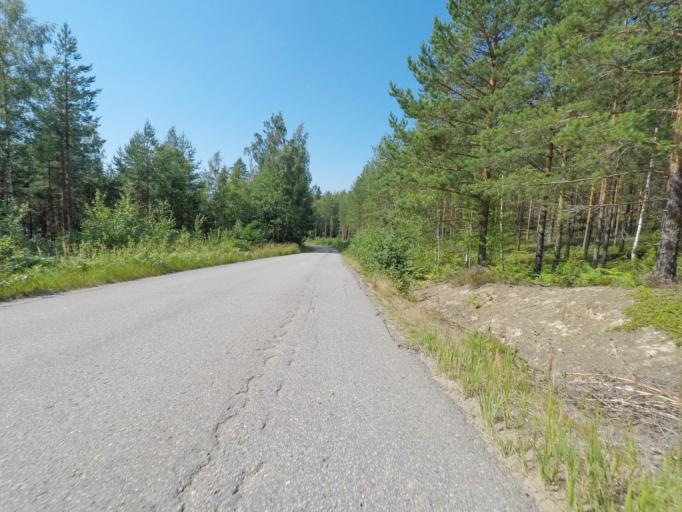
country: FI
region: Southern Savonia
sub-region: Mikkeli
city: Puumala
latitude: 61.4232
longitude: 28.1012
